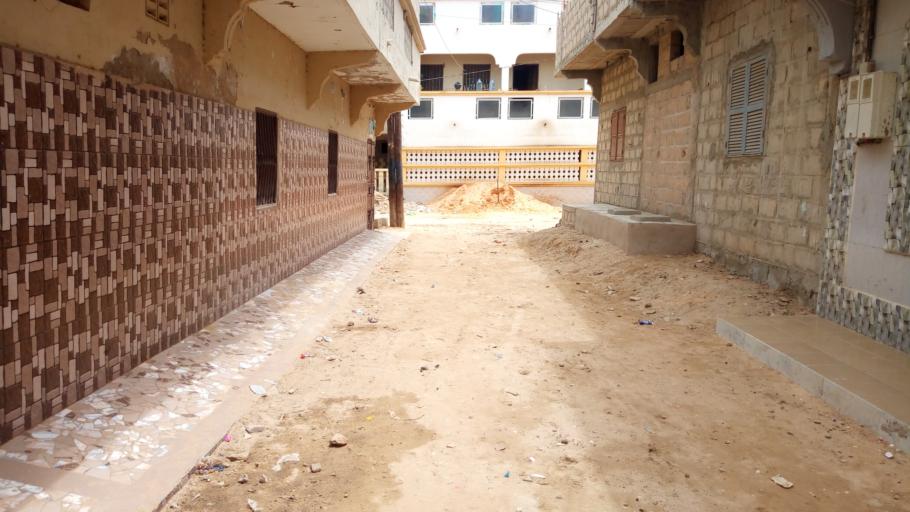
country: SN
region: Saint-Louis
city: Saint-Louis
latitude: 16.0141
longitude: -16.4858
